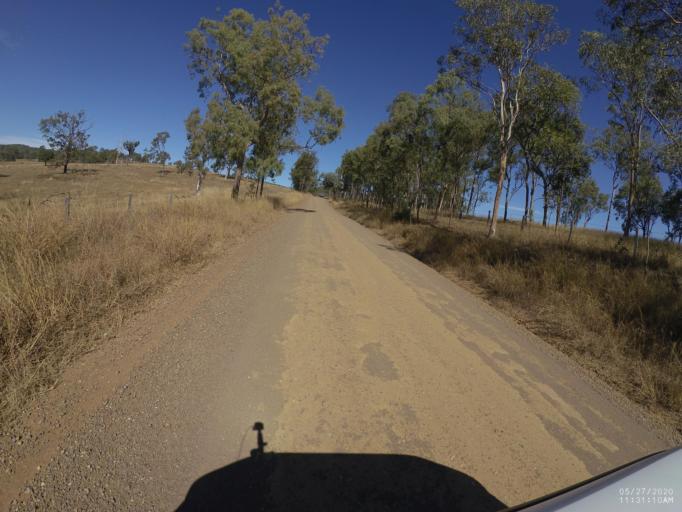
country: AU
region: Queensland
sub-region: Ipswich
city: Redbank Plains
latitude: -27.7414
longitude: 152.8310
